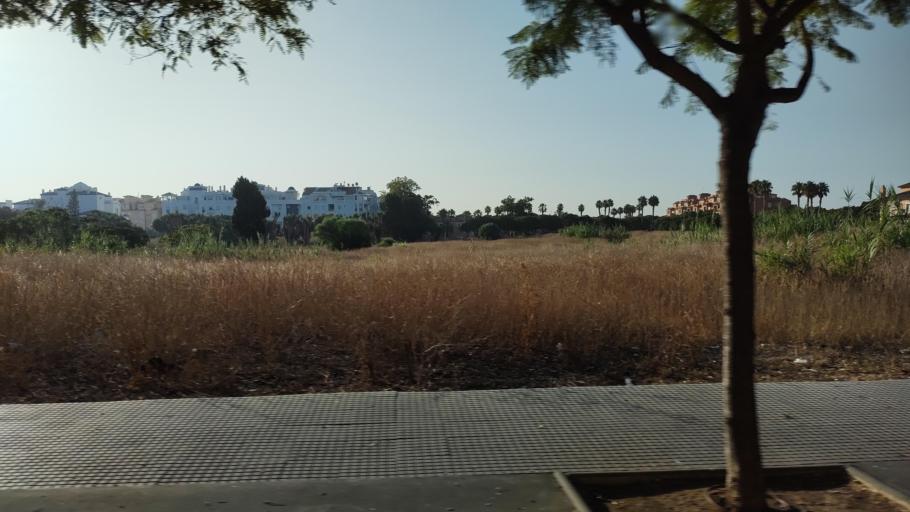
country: ES
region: Andalusia
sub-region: Provincia de Malaga
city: Torremolinos
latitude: 36.6419
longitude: -4.4867
